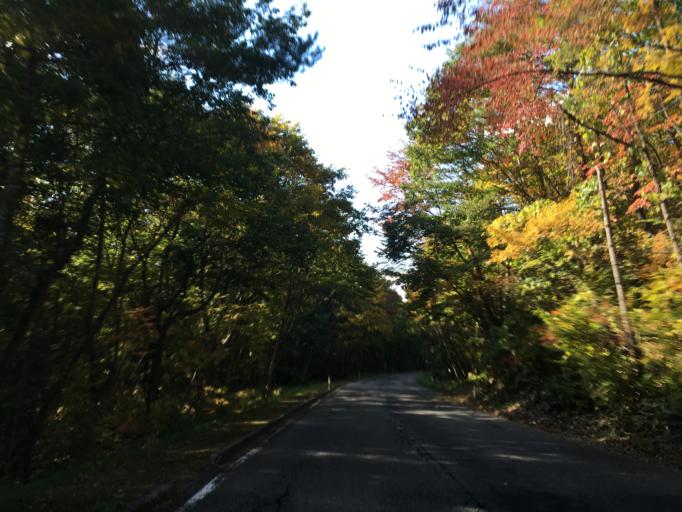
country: JP
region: Fukushima
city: Inawashiro
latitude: 37.6127
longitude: 140.2156
